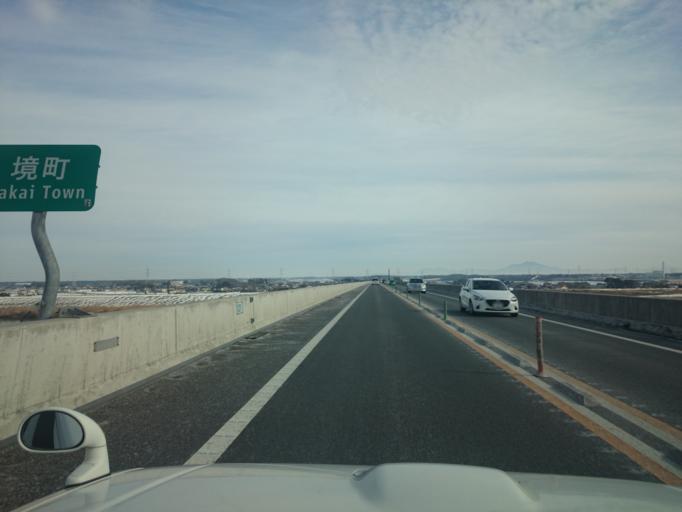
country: JP
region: Ibaraki
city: Sakai
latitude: 36.1160
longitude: 139.7663
